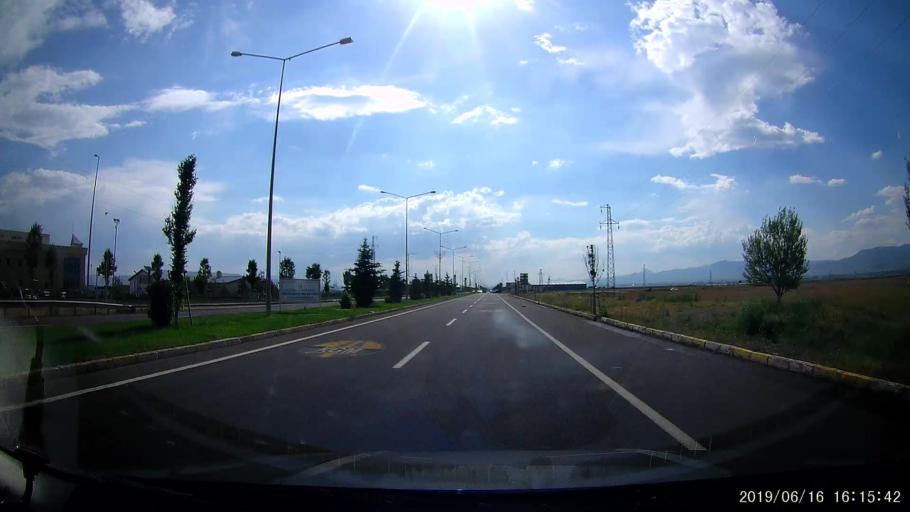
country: TR
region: Erzurum
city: Erzurum
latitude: 39.9622
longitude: 41.2209
